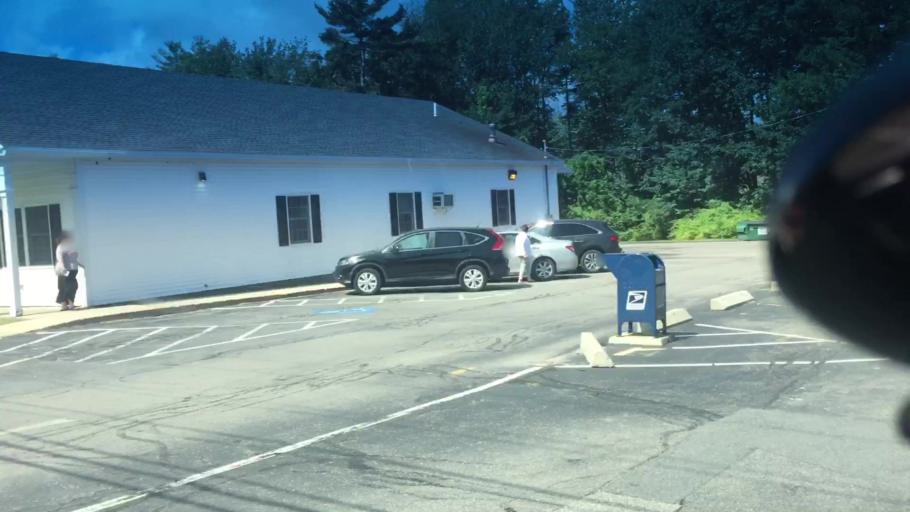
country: US
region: Maine
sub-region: York County
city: York Beach
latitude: 43.1733
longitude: -70.6150
